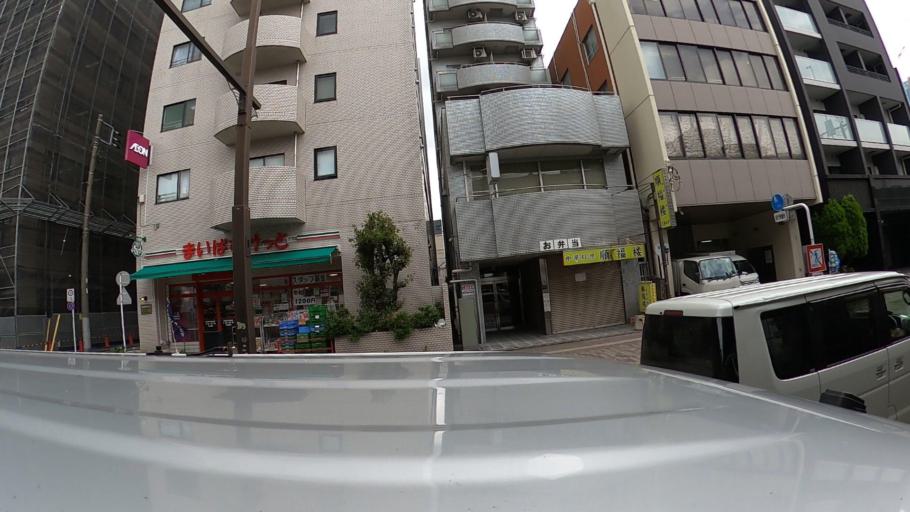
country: JP
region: Kanagawa
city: Yokohama
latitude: 35.4744
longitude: 139.6343
